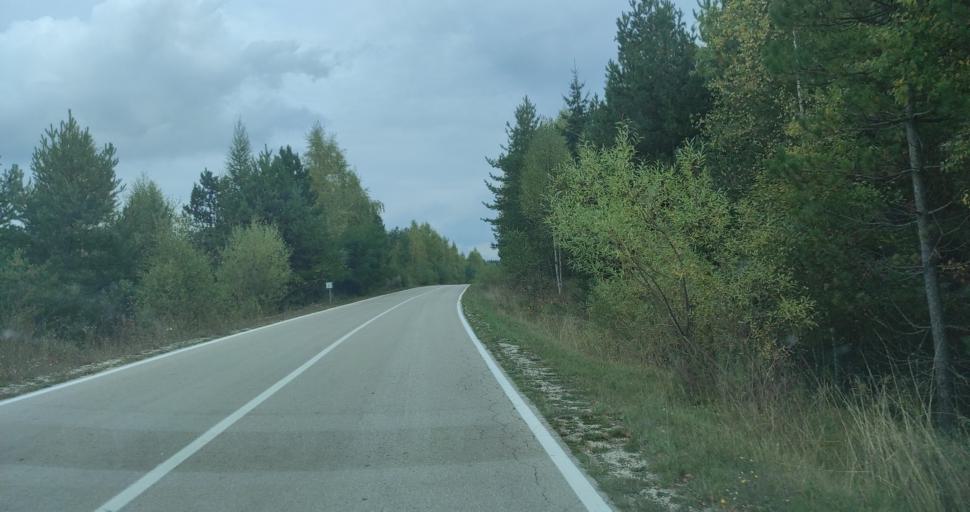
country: RS
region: Central Serbia
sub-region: Jablanicki Okrug
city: Crna Trava
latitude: 42.6902
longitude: 22.3175
